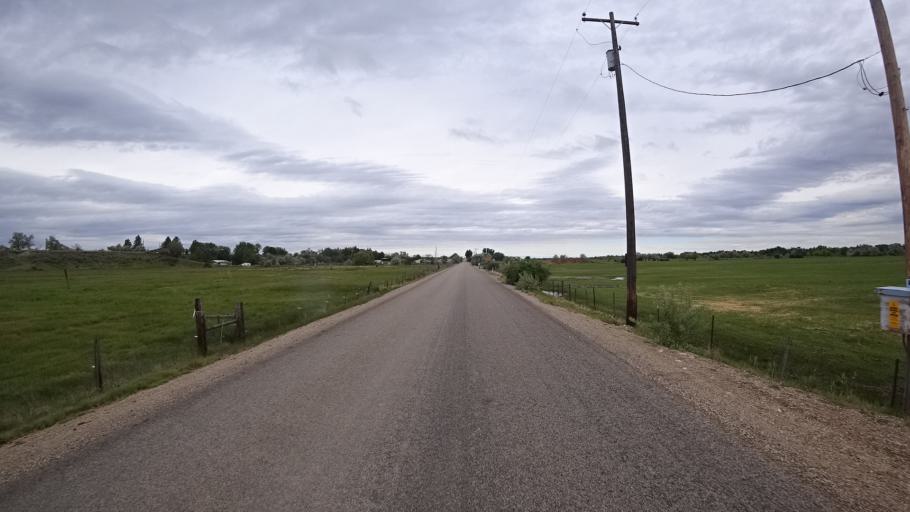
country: US
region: Idaho
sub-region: Ada County
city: Star
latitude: 43.6703
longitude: -116.4954
